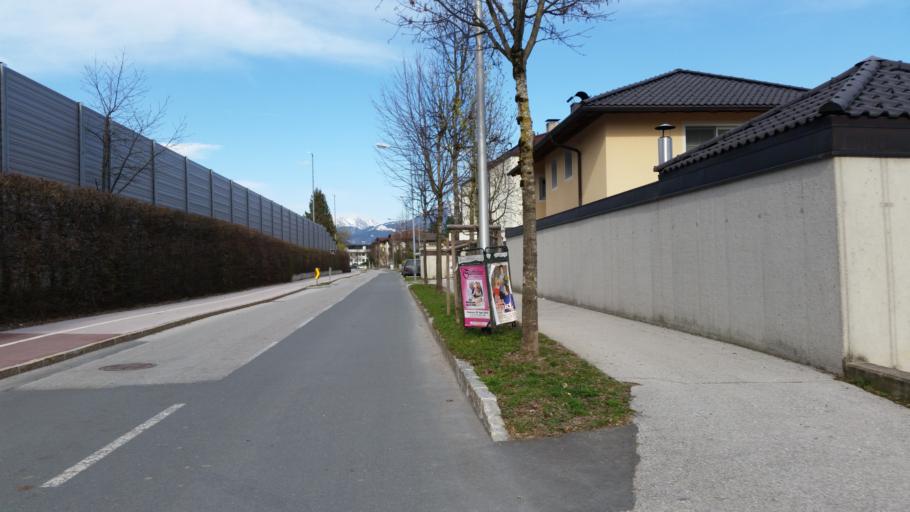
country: AT
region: Tyrol
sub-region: Politischer Bezirk Kufstein
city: Worgl
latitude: 47.4850
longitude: 12.0538
